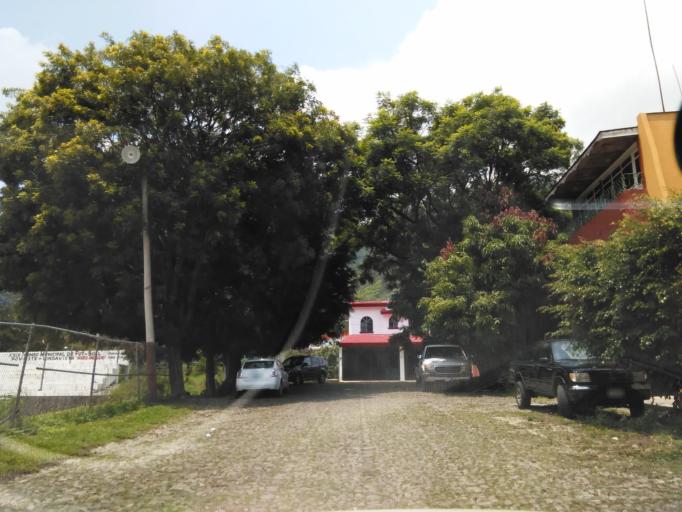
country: MX
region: Nayarit
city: Tepic
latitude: 21.5108
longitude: -104.9199
